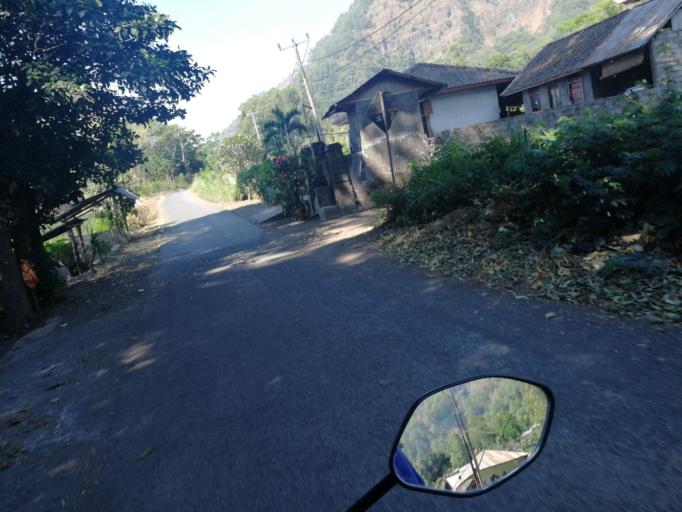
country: ID
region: Bali
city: Banjar Buahan
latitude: -8.2790
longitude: 115.4114
